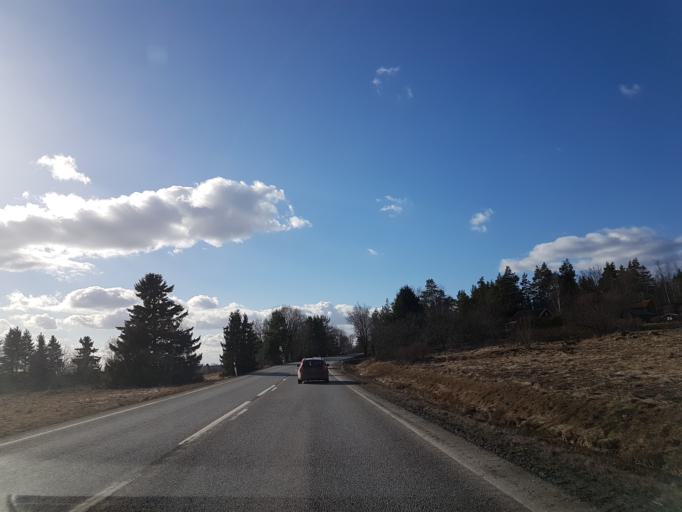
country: SE
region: Stockholm
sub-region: Norrtalje Kommun
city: Norrtalje
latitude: 59.7329
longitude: 18.5570
